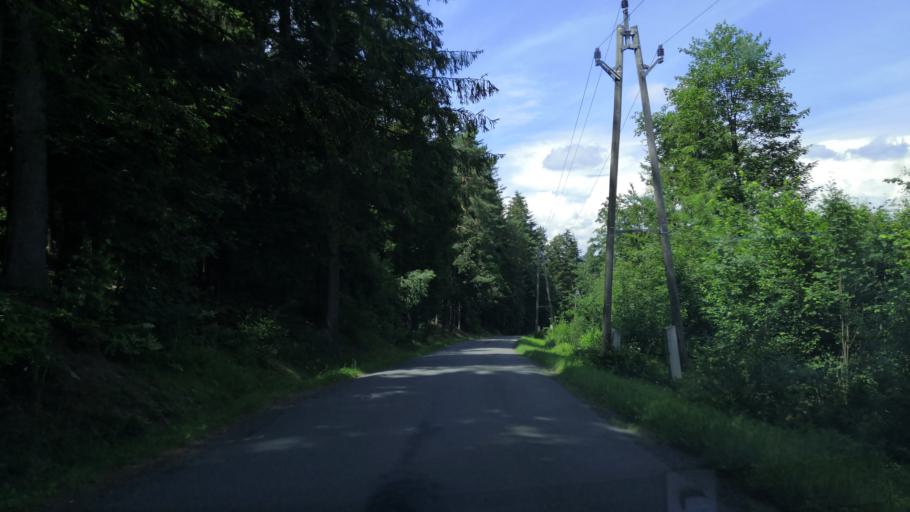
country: CZ
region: Zlin
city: Vidce
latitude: 49.4304
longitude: 18.0946
